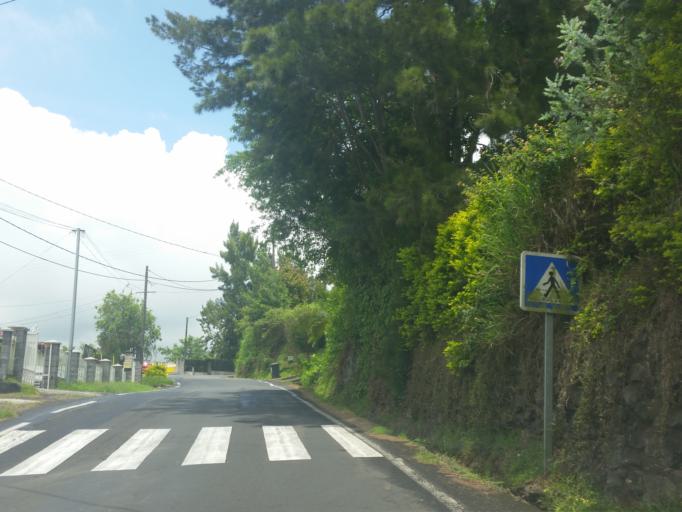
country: RE
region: Reunion
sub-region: Reunion
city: Le Tampon
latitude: -21.2426
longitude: 55.5114
